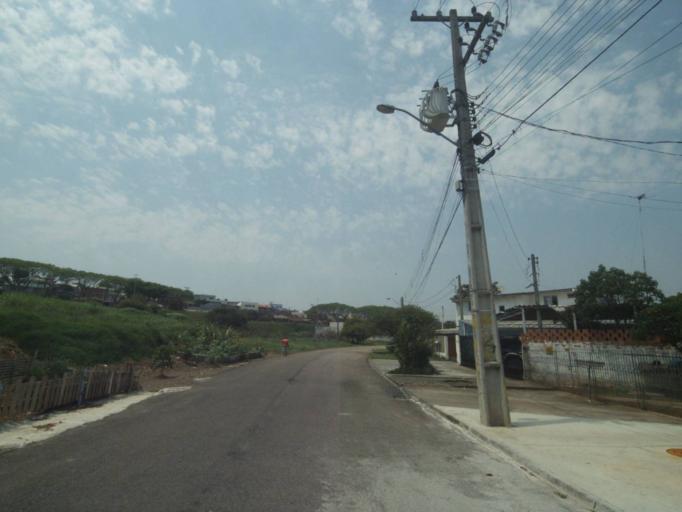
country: BR
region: Parana
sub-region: Sao Jose Dos Pinhais
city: Sao Jose dos Pinhais
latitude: -25.5325
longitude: -49.2525
